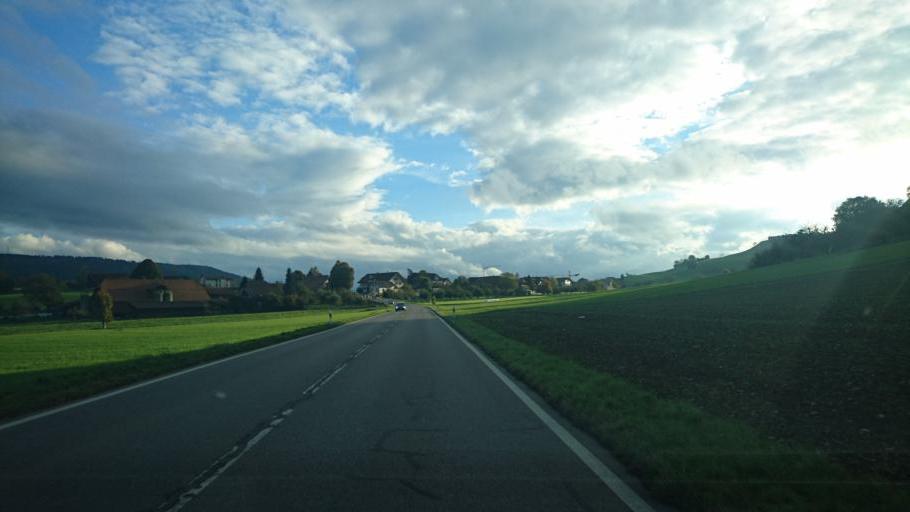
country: CH
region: Bern
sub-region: Bern-Mittelland District
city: Konolfingen
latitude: 46.8946
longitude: 7.6335
